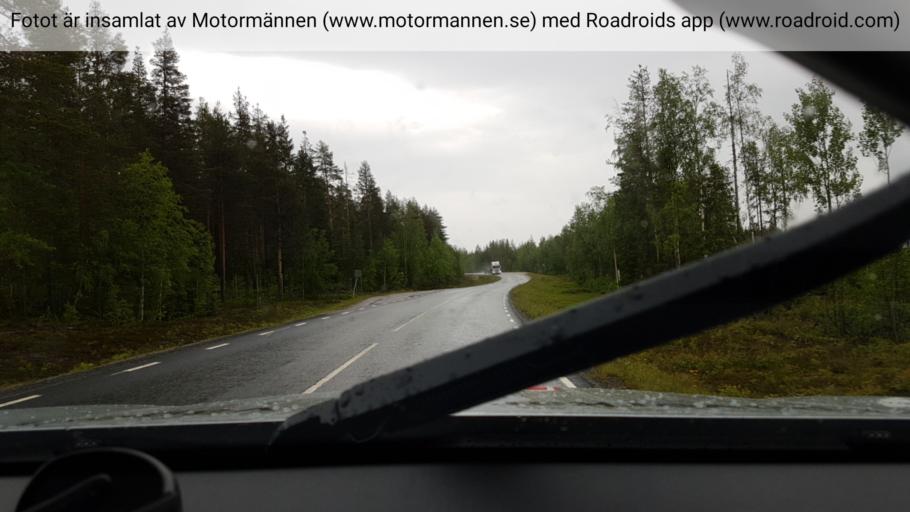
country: SE
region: Vaesterbotten
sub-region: Sorsele Kommun
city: Sorsele
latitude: 65.2887
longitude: 17.8241
